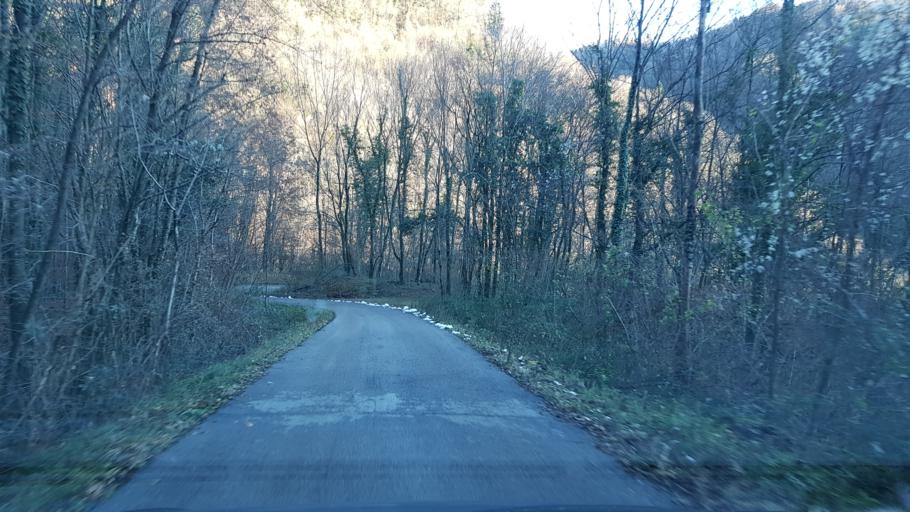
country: IT
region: Friuli Venezia Giulia
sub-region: Provincia di Udine
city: Savogna
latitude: 46.1807
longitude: 13.5366
